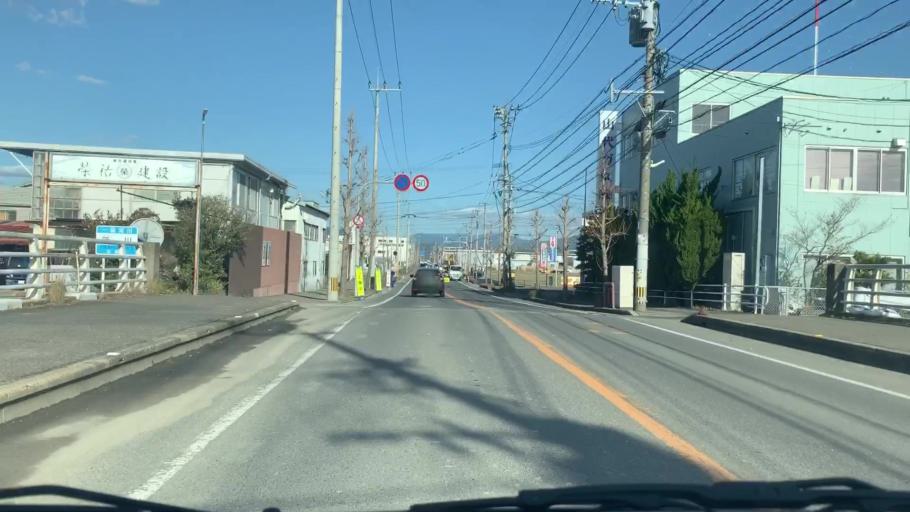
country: JP
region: Saga Prefecture
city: Saga-shi
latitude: 33.2502
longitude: 130.2651
